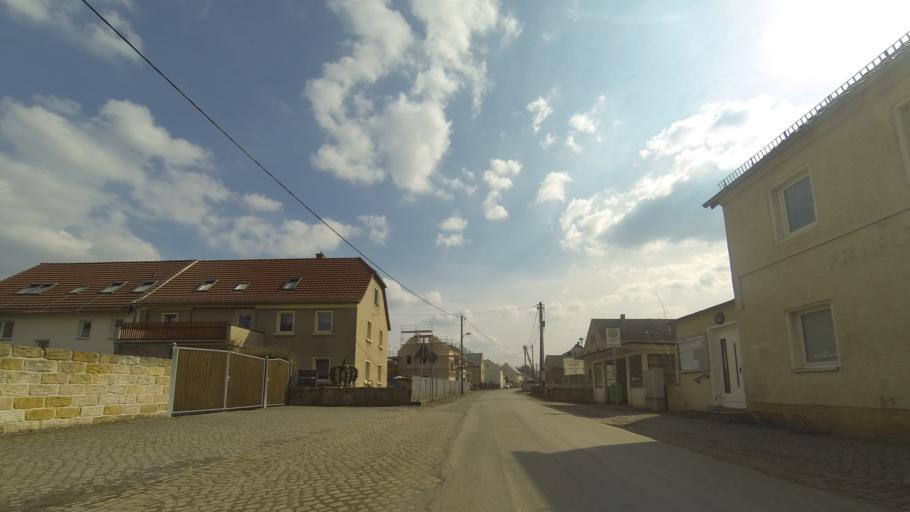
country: DE
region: Saxony
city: Moritzburg
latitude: 51.1478
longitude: 13.7394
